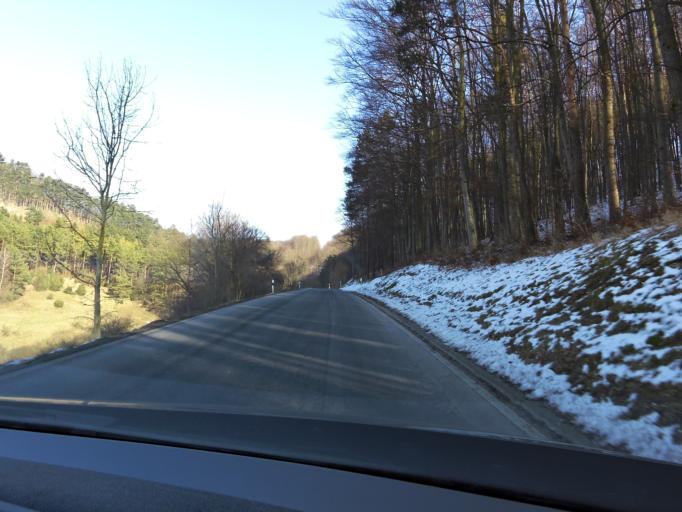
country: DE
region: Hesse
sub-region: Regierungsbezirk Kassel
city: Sontra
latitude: 51.0770
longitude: 10.0065
